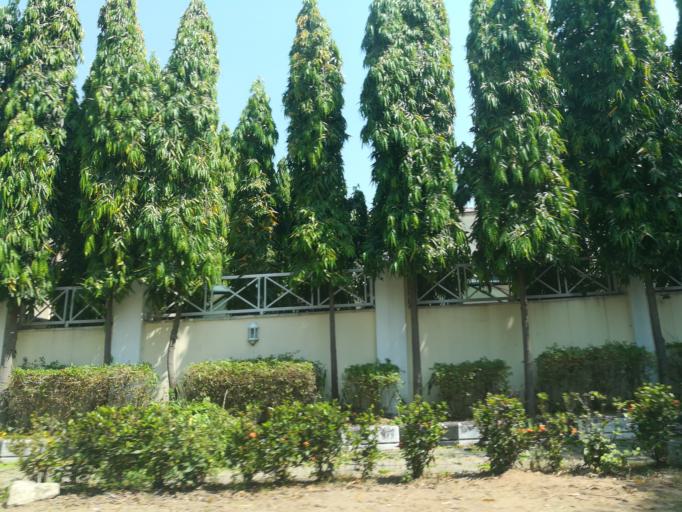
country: NG
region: Abuja Federal Capital Territory
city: Abuja
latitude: 9.0635
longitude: 7.4215
